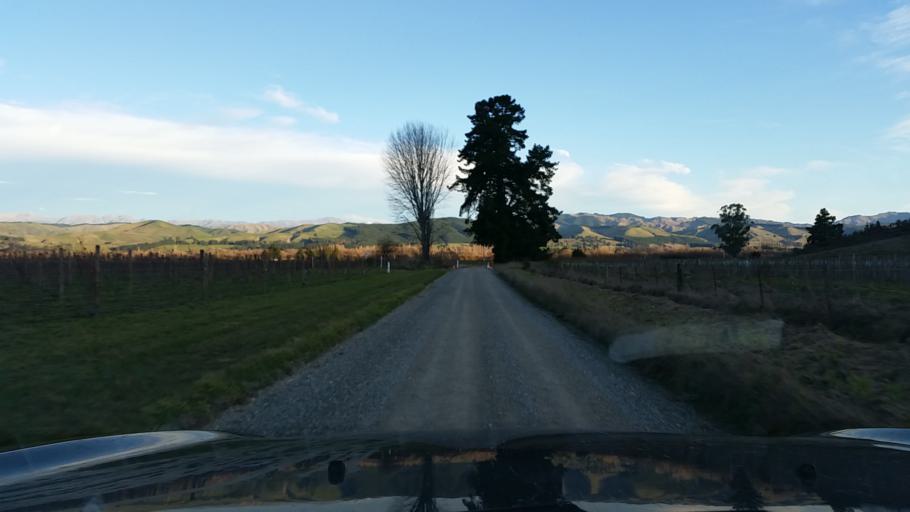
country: NZ
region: Marlborough
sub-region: Marlborough District
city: Blenheim
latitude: -41.5149
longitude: 173.5849
